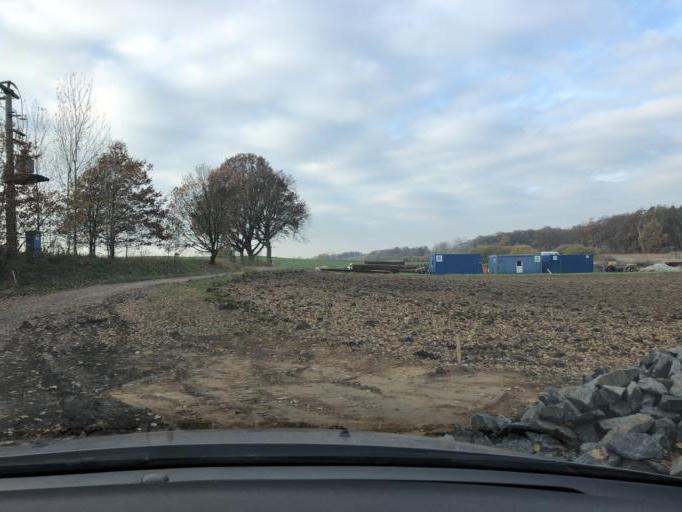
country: DE
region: Saxony
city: Mutzschen
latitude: 51.2784
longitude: 12.8996
